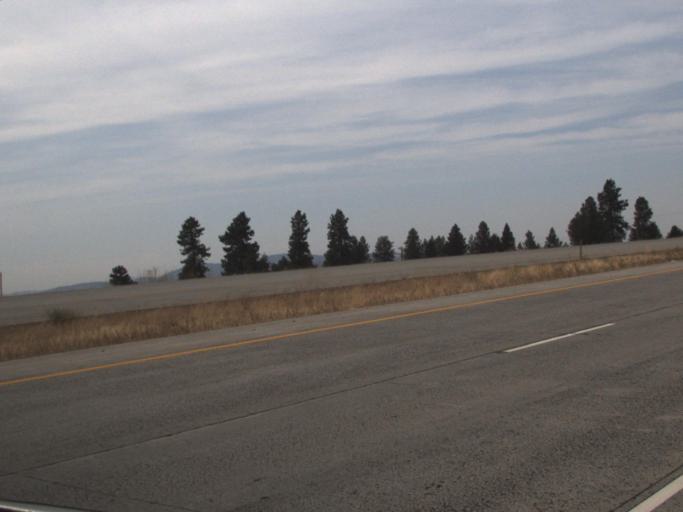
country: US
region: Washington
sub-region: Spokane County
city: Mead
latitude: 47.7379
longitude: -117.3604
